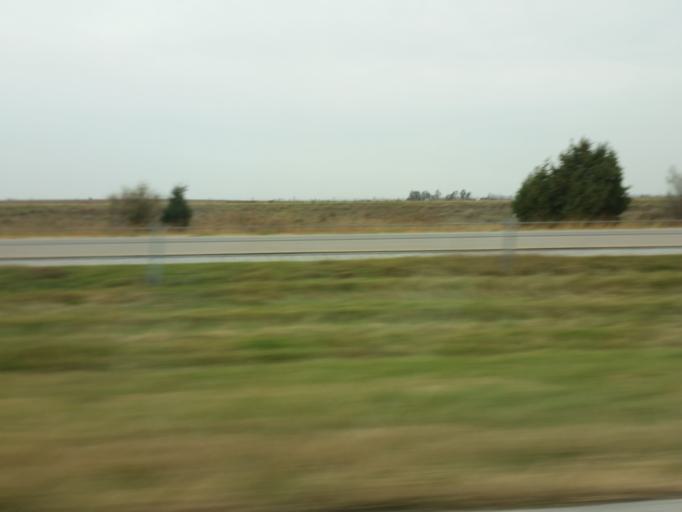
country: US
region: Iowa
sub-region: Scott County
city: Walcott
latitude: 41.6223
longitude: -90.8053
